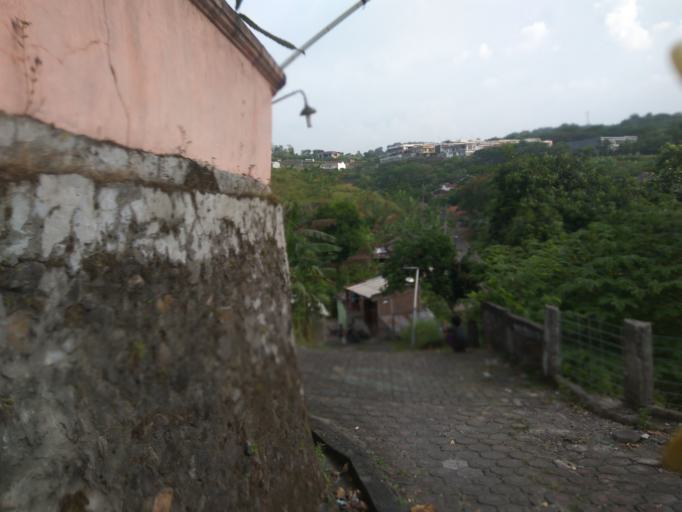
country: ID
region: Central Java
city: Semarang
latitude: -7.0201
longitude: 110.4425
